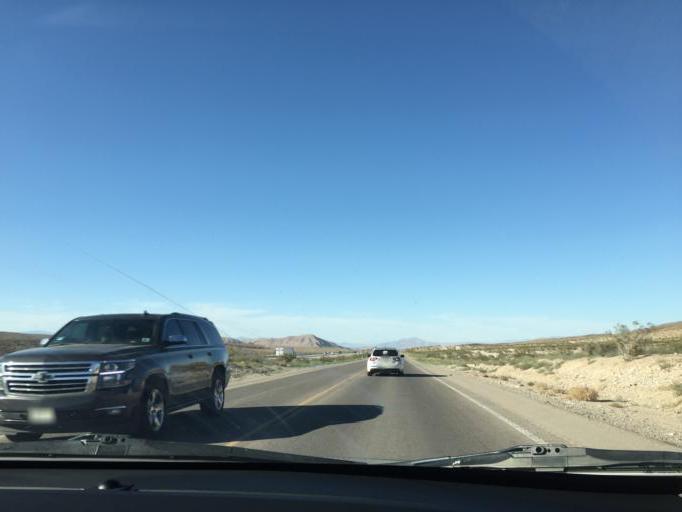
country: US
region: Nevada
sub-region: Clark County
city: Enterprise
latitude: 35.8877
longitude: -115.2226
